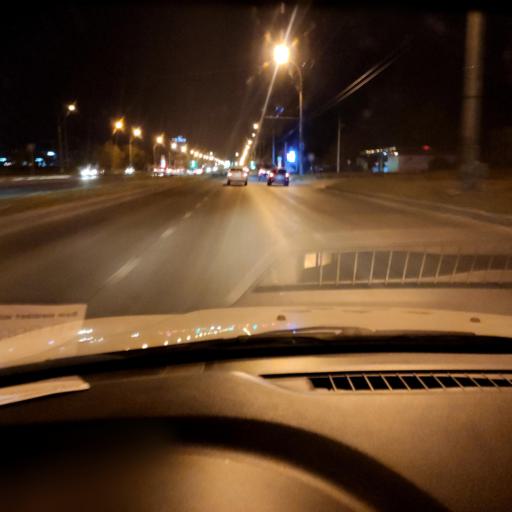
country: RU
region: Samara
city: Tol'yatti
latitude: 53.5397
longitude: 49.2640
